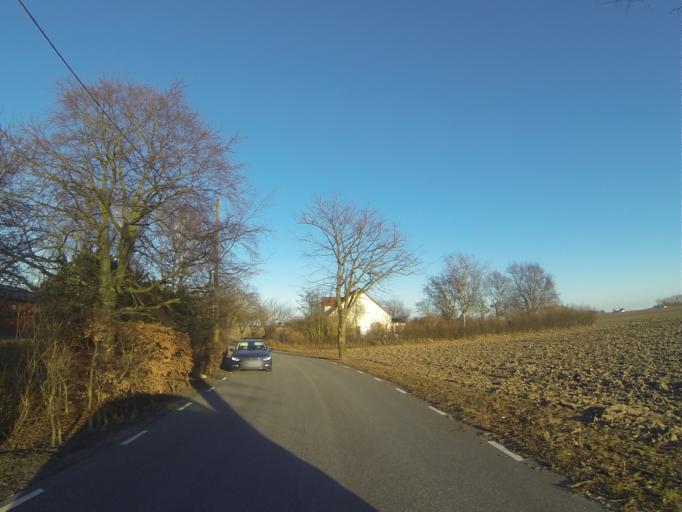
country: SE
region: Skane
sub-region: Malmo
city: Tygelsjo
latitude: 55.5425
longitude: 13.0207
